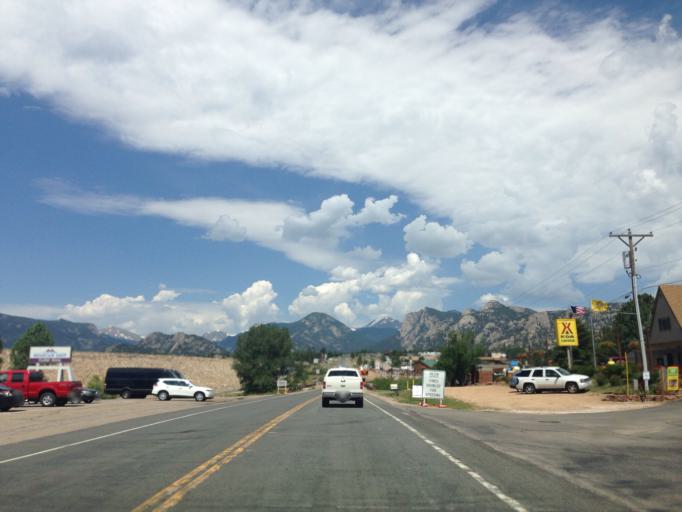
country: US
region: Colorado
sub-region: Larimer County
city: Estes Park
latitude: 40.3777
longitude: -105.4869
